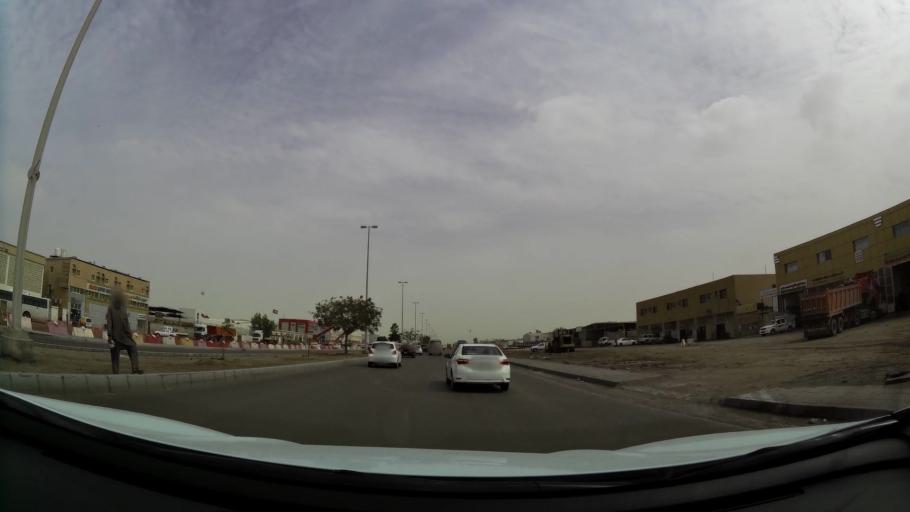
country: AE
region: Abu Dhabi
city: Abu Dhabi
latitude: 24.3593
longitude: 54.5040
